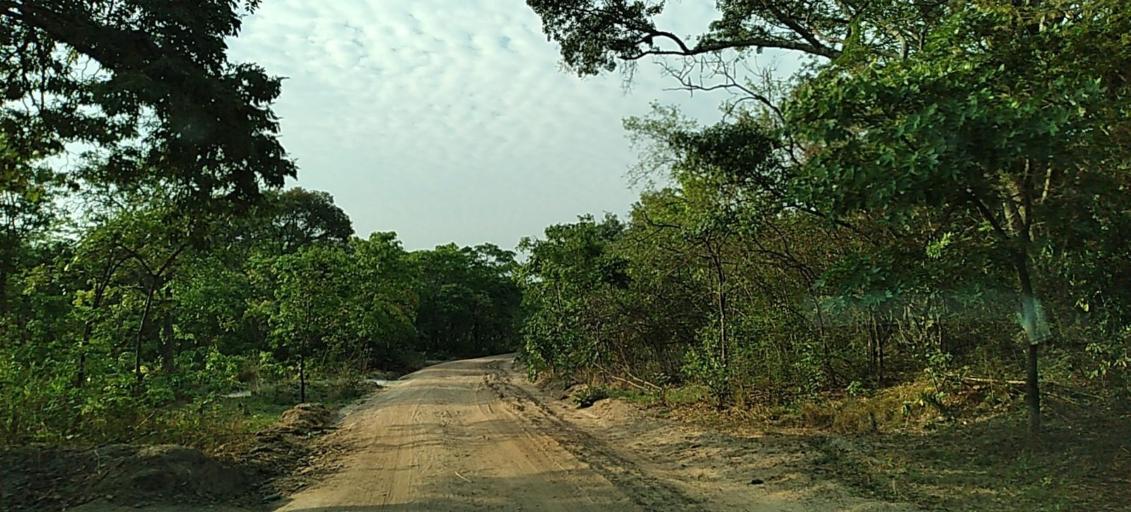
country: ZM
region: Copperbelt
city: Chingola
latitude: -12.8777
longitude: 27.6916
